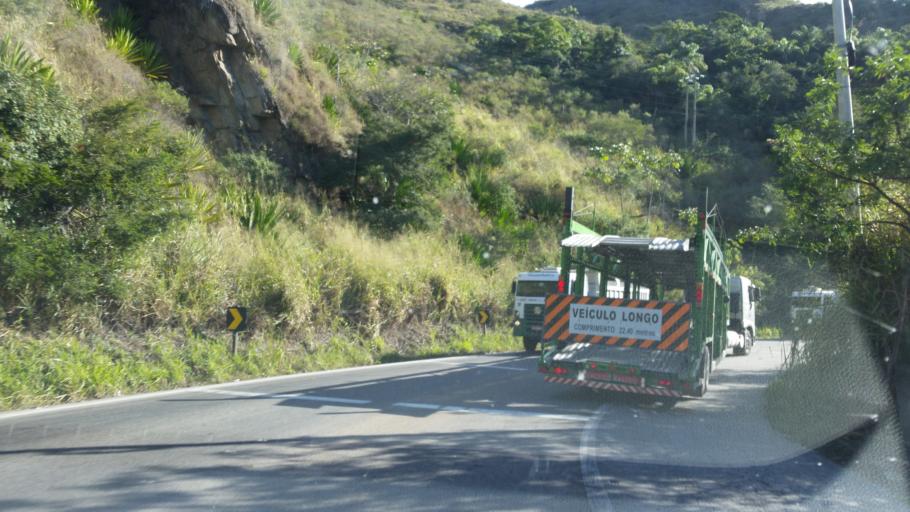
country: BR
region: Sao Paulo
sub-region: Sao Sebastiao
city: Sao Sebastiao
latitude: -23.7276
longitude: -45.4072
